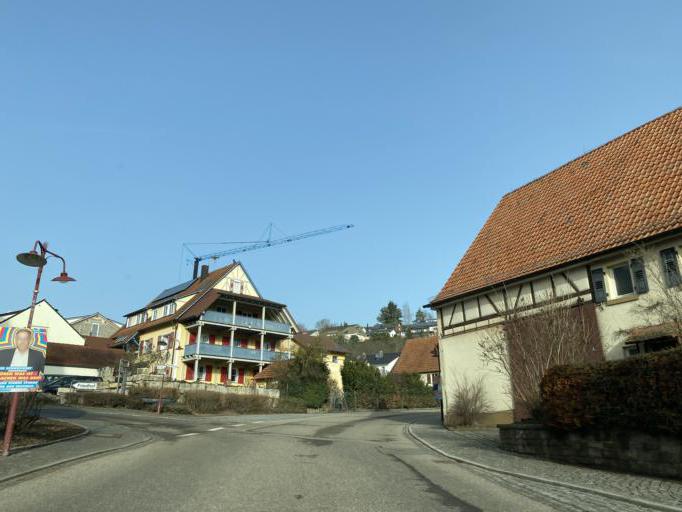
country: DE
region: Baden-Wuerttemberg
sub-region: Karlsruhe Region
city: Monsheim
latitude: 48.8871
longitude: 8.8975
